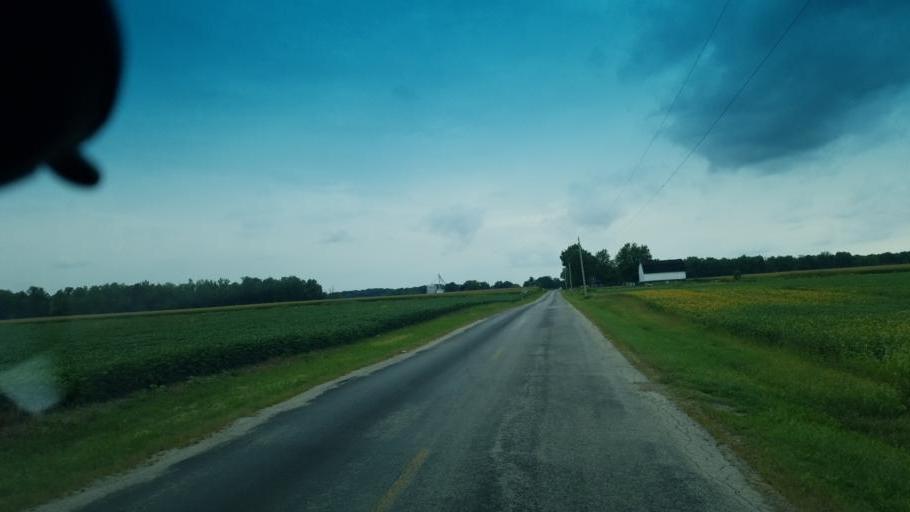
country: US
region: Ohio
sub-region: Richland County
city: Shelby
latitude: 40.9085
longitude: -82.7071
